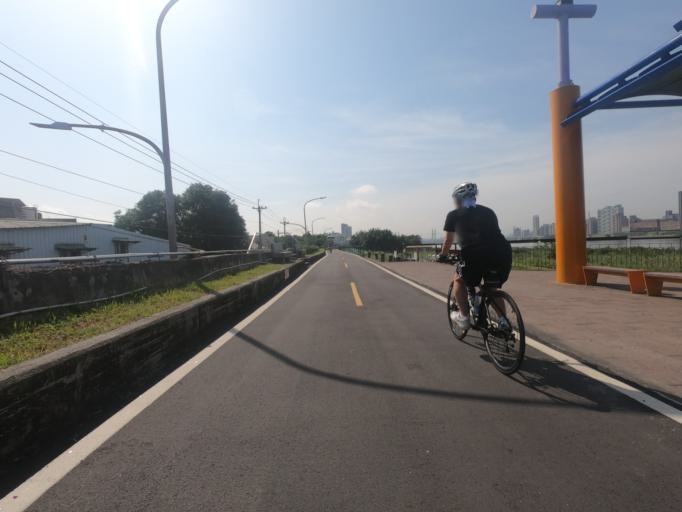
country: TW
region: Taipei
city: Taipei
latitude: 25.0978
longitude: 121.4921
